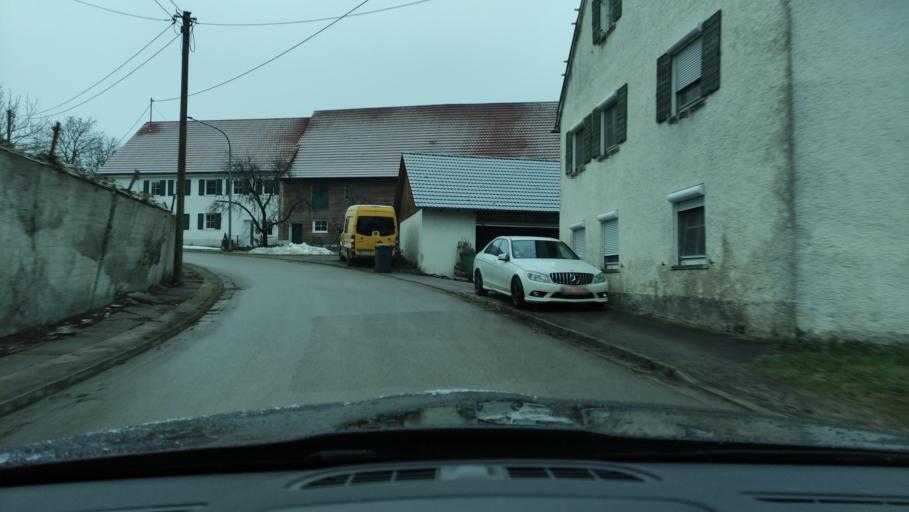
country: DE
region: Bavaria
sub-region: Swabia
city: Deisenhausen
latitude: 48.2646
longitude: 10.3284
